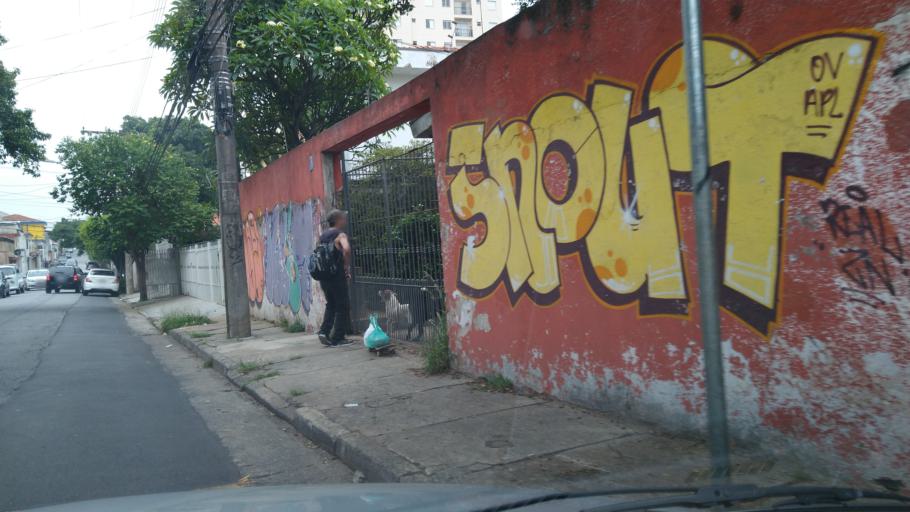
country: BR
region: Sao Paulo
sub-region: Guarulhos
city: Guarulhos
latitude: -23.4873
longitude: -46.5907
